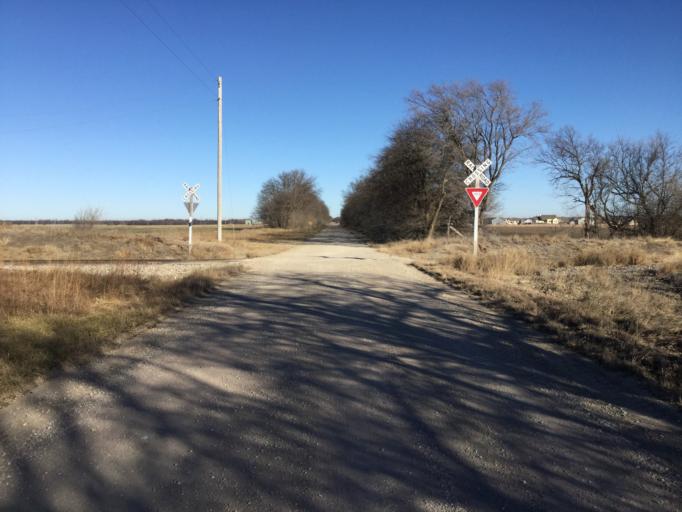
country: US
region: Kansas
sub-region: Butler County
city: Andover
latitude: 37.7885
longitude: -97.1171
